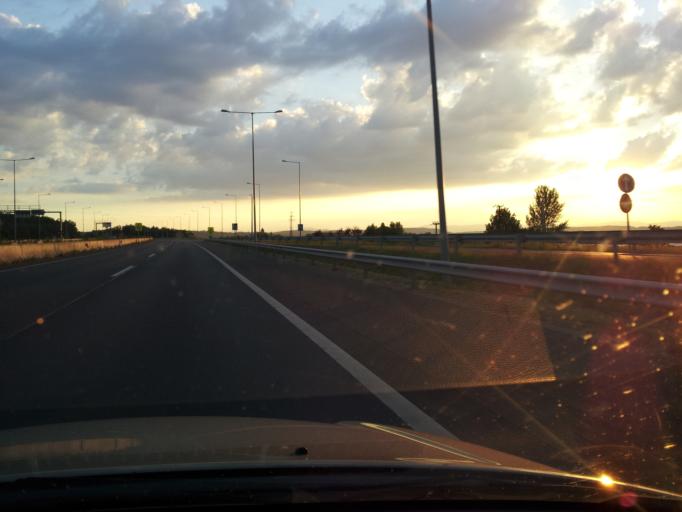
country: HU
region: Pest
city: Szada
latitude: 47.6130
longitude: 19.3139
